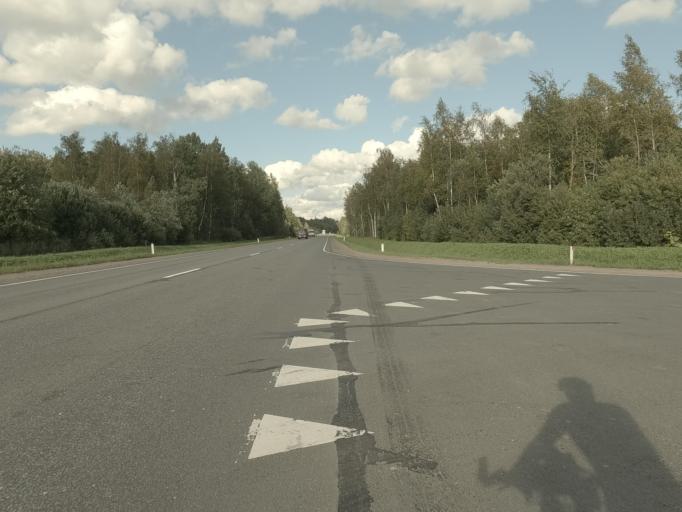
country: RU
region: Leningrad
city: Nikol'skoye
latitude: 59.6626
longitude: 30.8761
